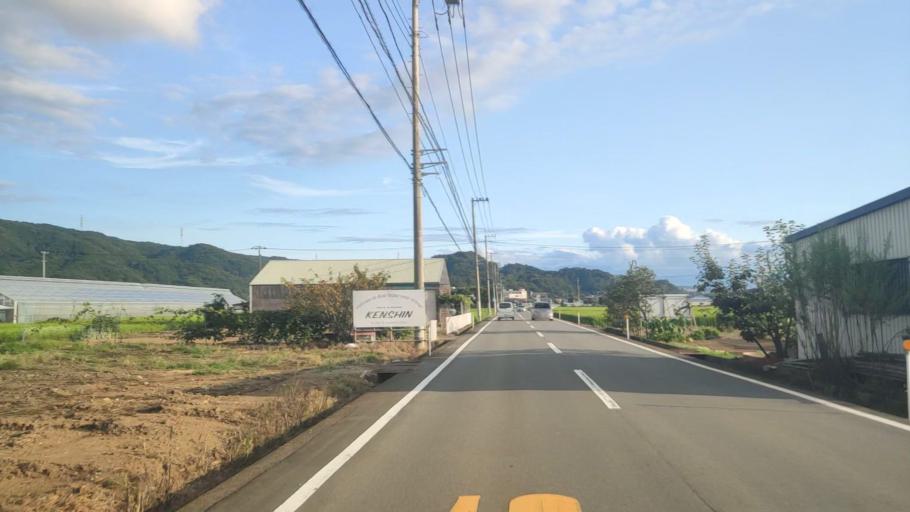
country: JP
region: Shizuoka
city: Mishima
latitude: 35.0629
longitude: 138.9522
